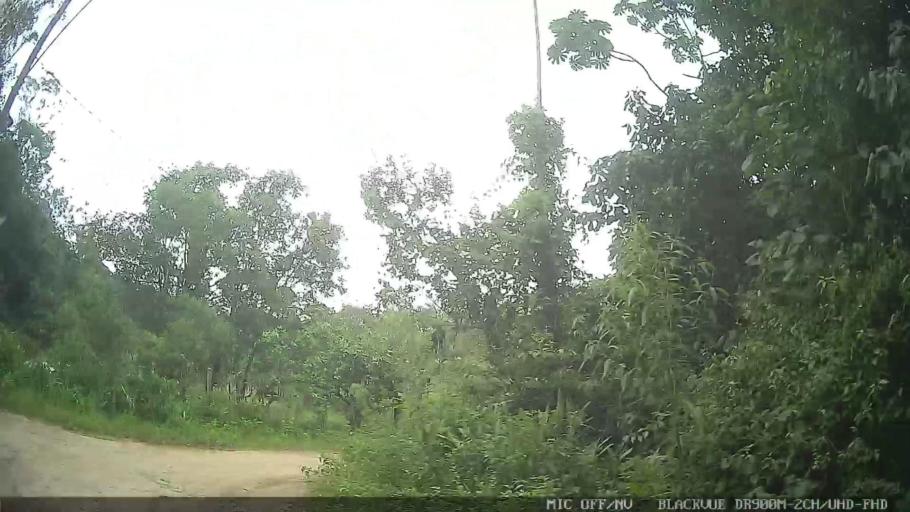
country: BR
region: Sao Paulo
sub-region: Aruja
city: Aruja
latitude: -23.4020
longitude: -46.2389
